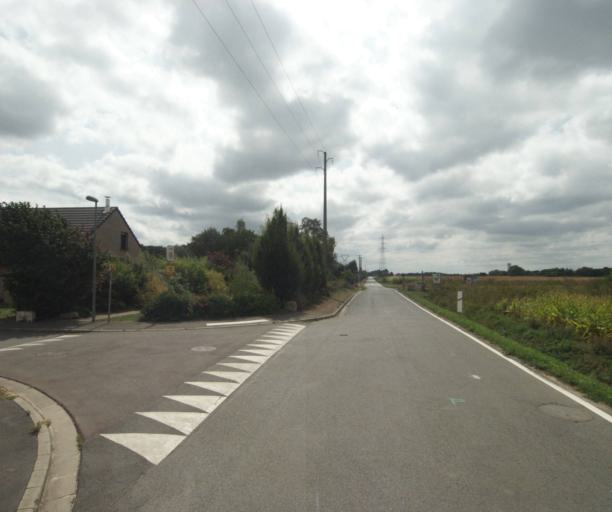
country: FR
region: Nord-Pas-de-Calais
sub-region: Departement du Nord
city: Tressin
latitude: 50.6177
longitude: 3.1875
